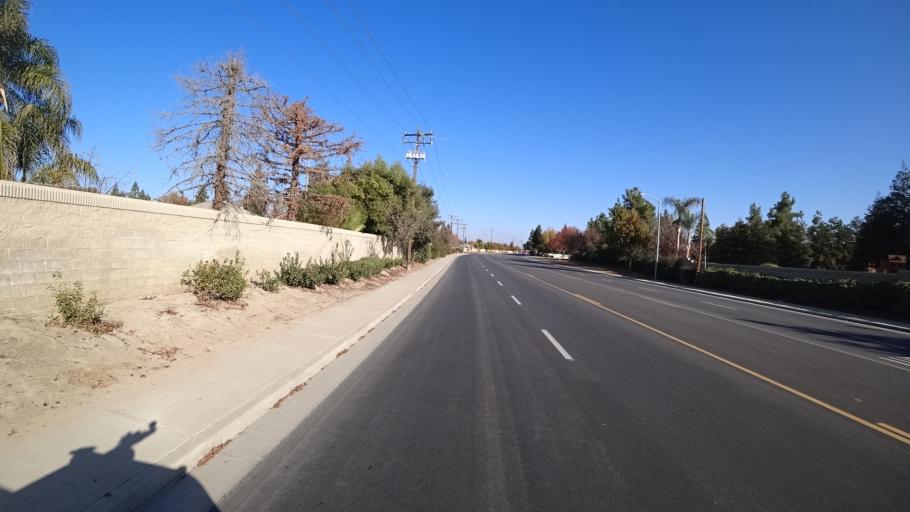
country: US
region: California
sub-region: Kern County
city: Greenacres
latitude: 35.3178
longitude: -119.1205
